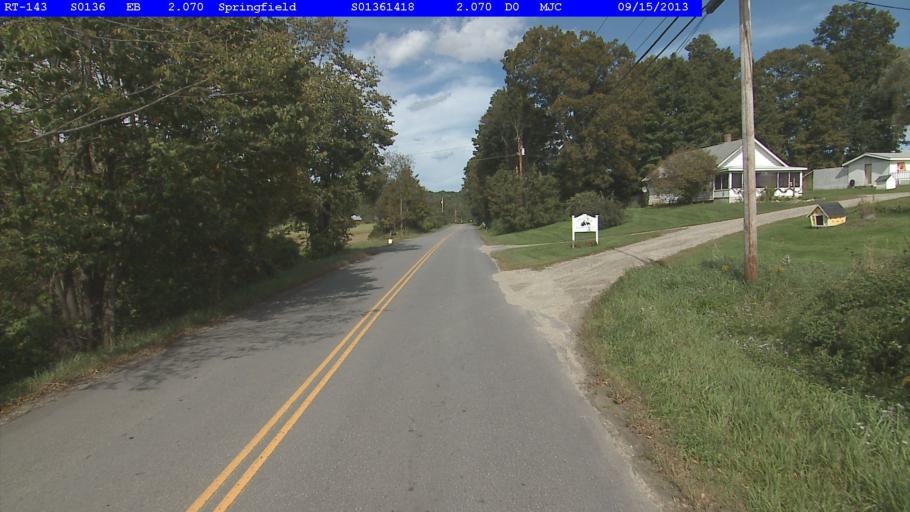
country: US
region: Vermont
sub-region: Windsor County
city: Springfield
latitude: 43.2943
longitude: -72.4492
